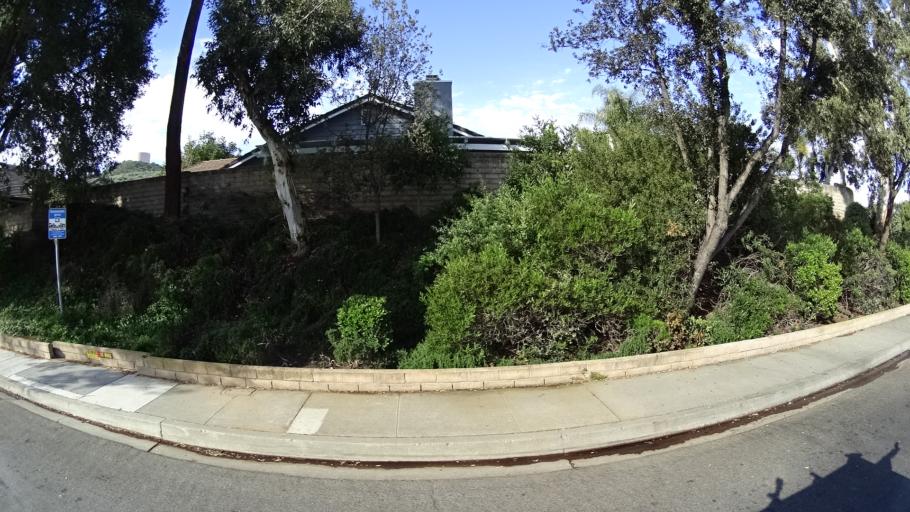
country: US
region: California
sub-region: Ventura County
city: Casa Conejo
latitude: 34.1723
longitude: -118.9505
